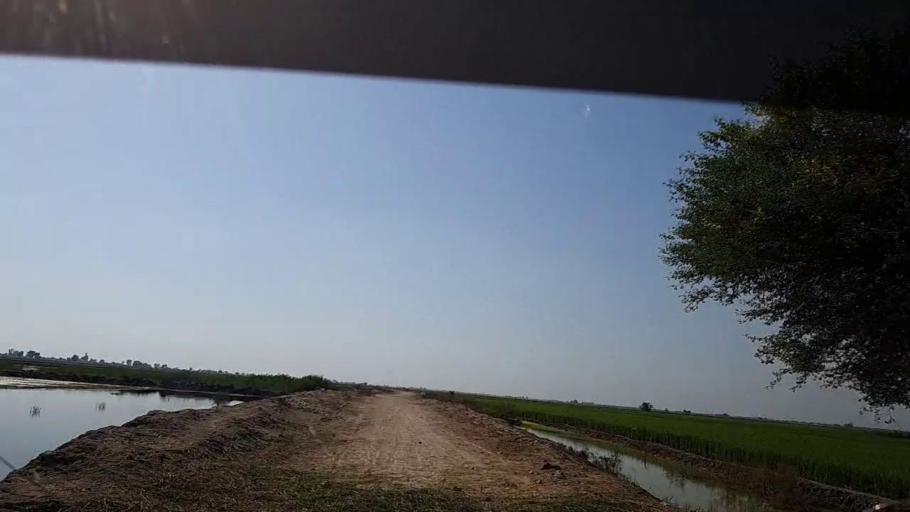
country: PK
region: Sindh
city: Tangwani
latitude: 28.3527
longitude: 69.0452
